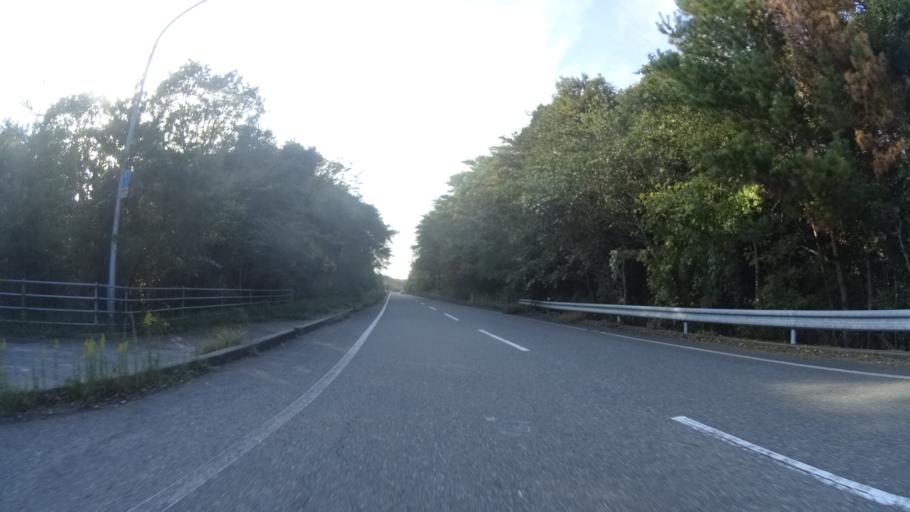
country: JP
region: Ishikawa
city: Hakui
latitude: 37.0710
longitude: 136.7426
